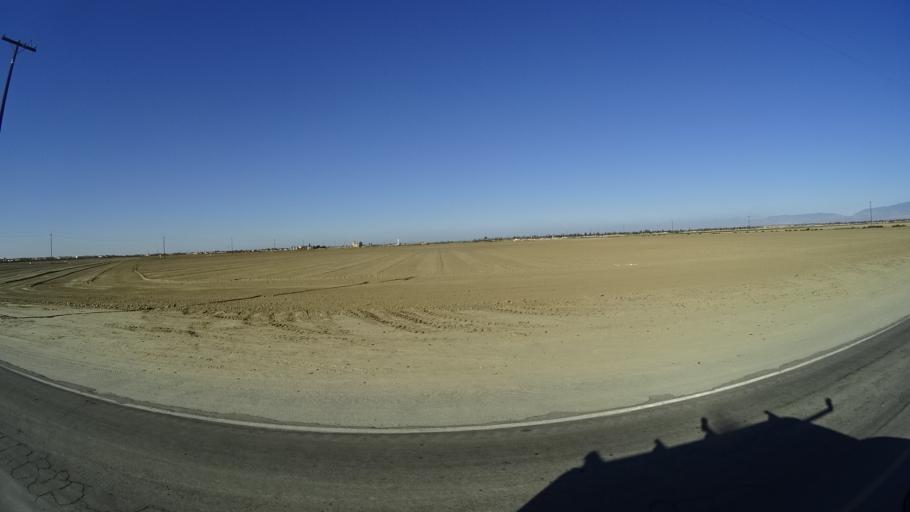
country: US
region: California
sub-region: Kern County
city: Greenfield
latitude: 35.2817
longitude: -119.0937
